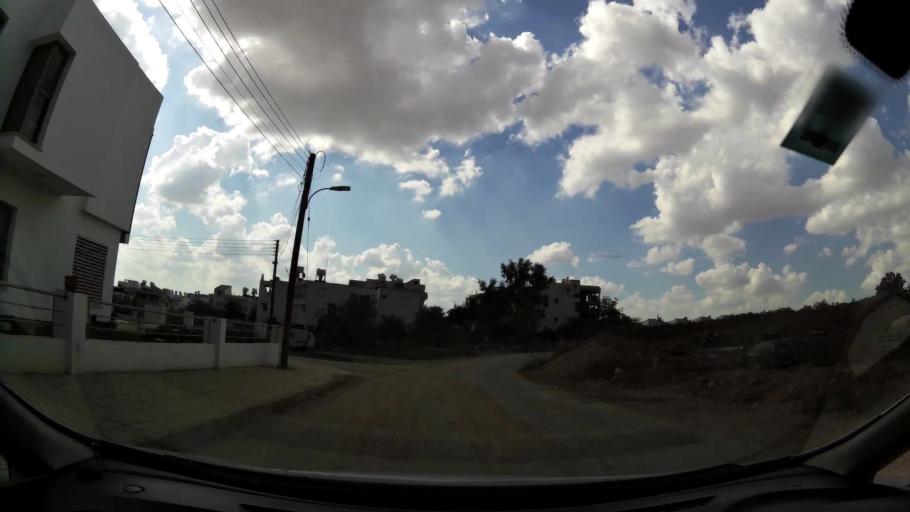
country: CY
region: Lefkosia
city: Nicosia
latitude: 35.2212
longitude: 33.3745
